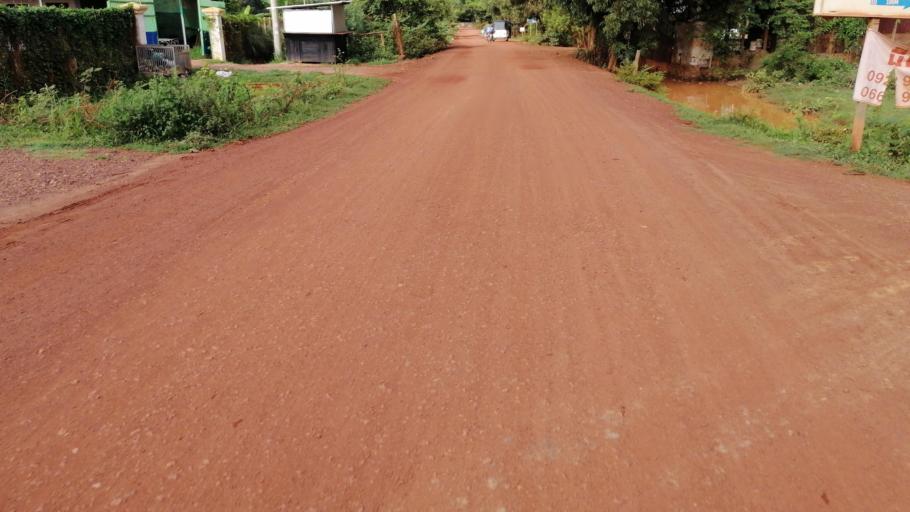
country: KH
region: Siem Reap
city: Siem Reap
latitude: 13.3603
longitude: 103.8293
